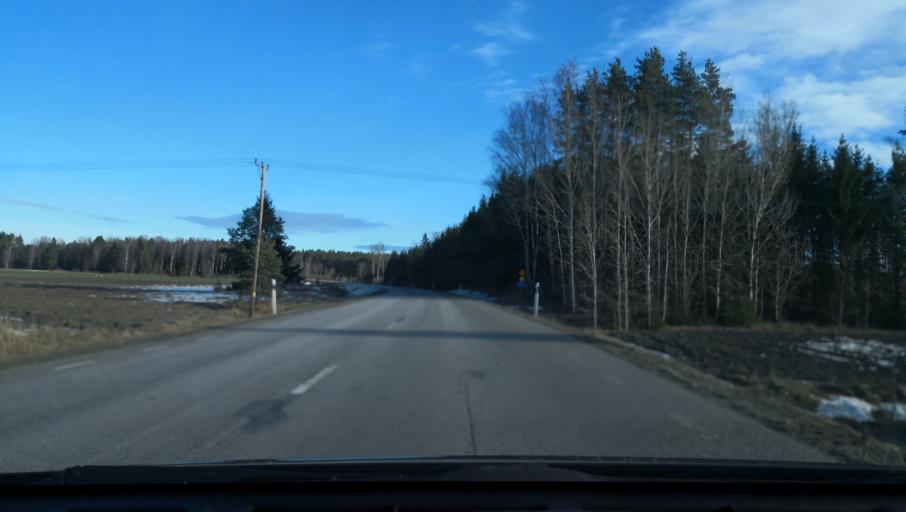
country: SE
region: Uppsala
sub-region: Osthammars Kommun
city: Osterbybruk
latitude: 60.1619
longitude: 17.9871
